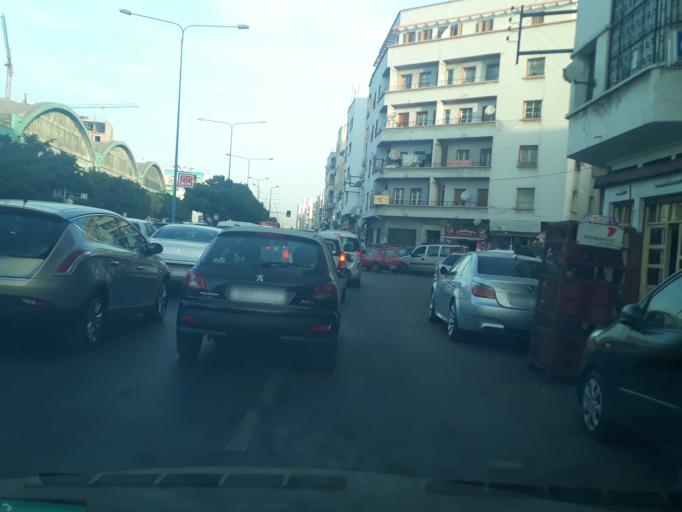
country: MA
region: Grand Casablanca
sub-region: Casablanca
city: Casablanca
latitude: 33.5785
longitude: -7.6343
